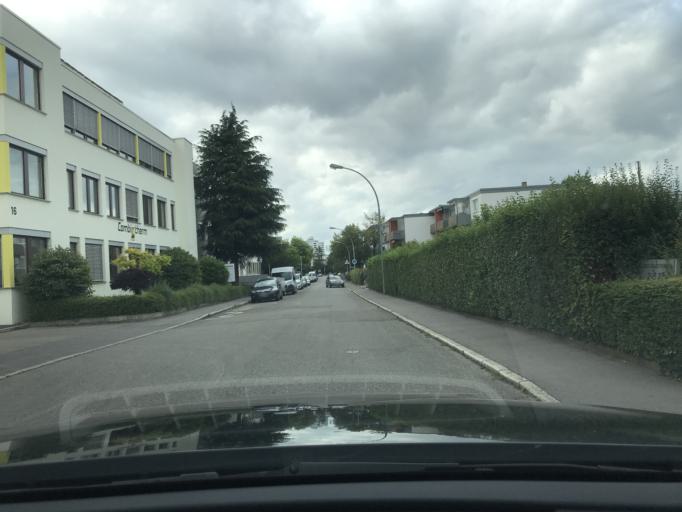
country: DE
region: Baden-Wuerttemberg
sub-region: Regierungsbezirk Stuttgart
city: Fellbach
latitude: 48.8289
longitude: 9.2617
